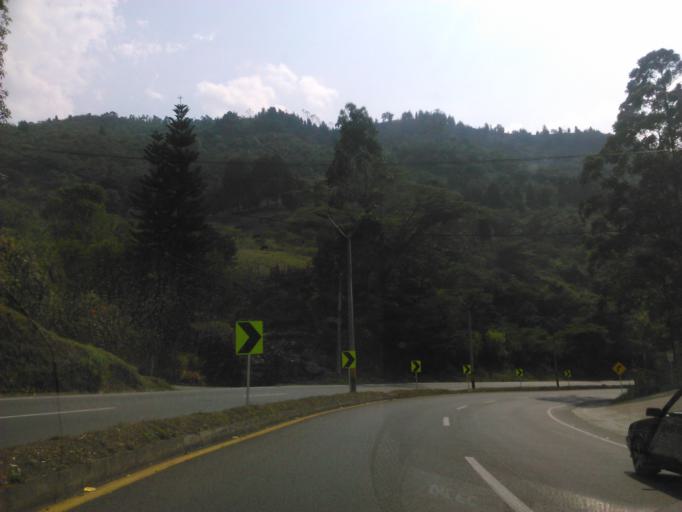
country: CO
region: Antioquia
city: Bello
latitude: 6.3175
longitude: -75.5299
